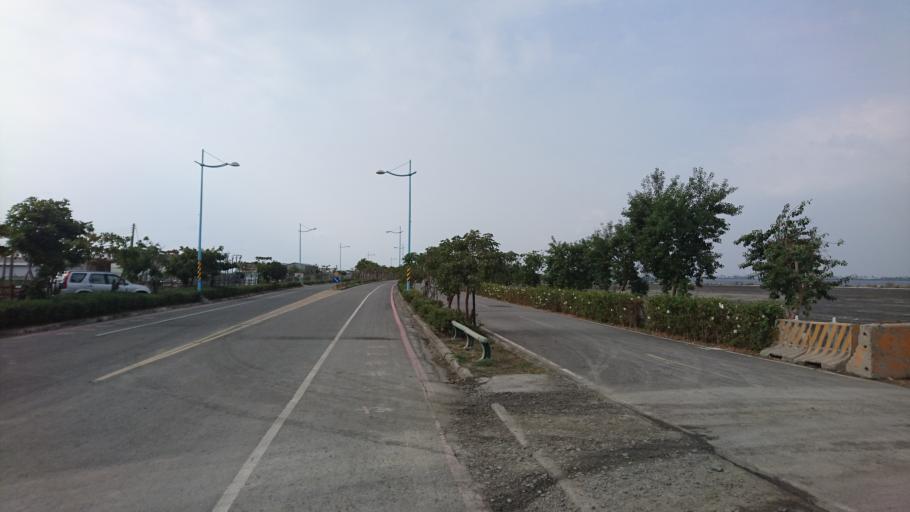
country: TW
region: Taiwan
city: Fengshan
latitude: 22.4343
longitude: 120.4809
